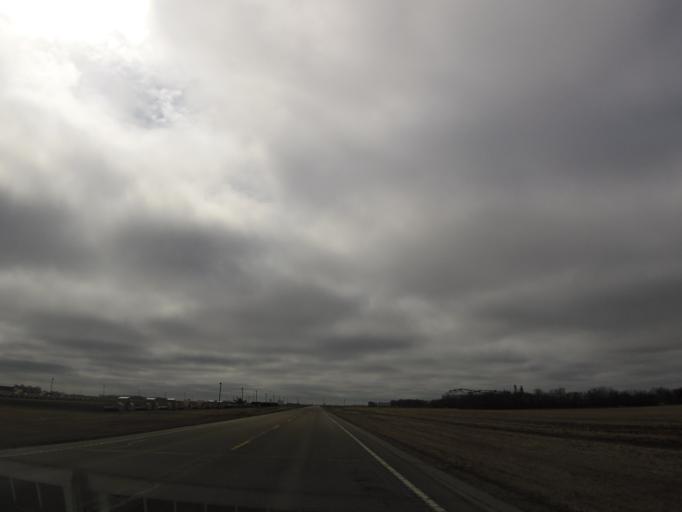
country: US
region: North Dakota
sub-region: Cass County
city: Casselton
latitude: 47.0121
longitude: -97.2138
